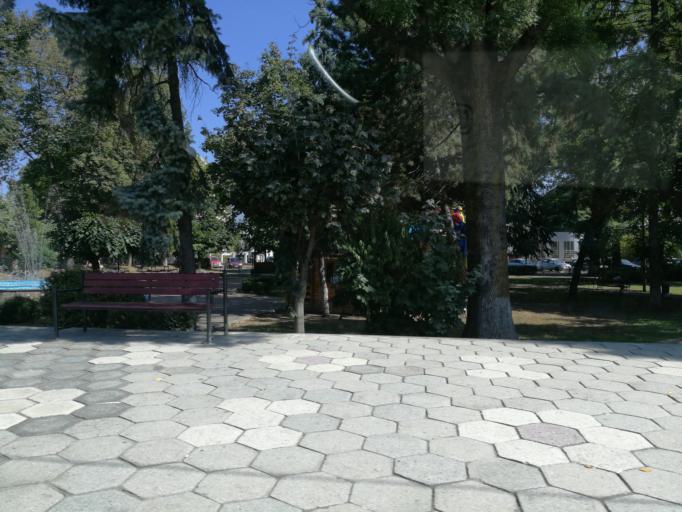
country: RO
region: Suceava
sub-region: Municipiul Suceava
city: Radauti
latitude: 47.8441
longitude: 25.9169
